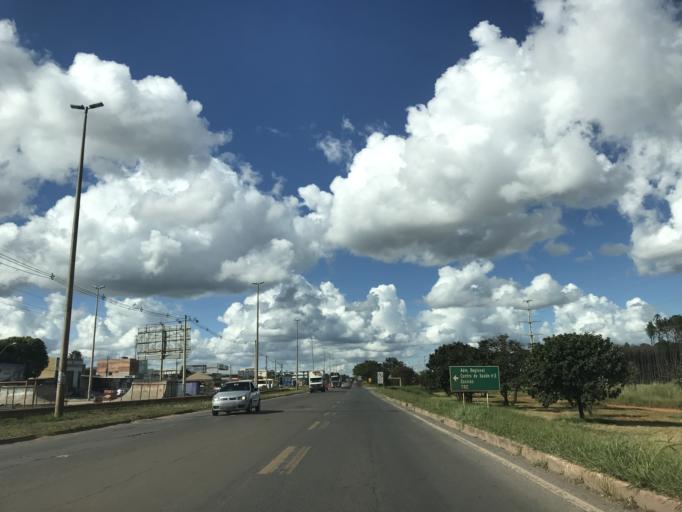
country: BR
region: Federal District
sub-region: Brasilia
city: Brasilia
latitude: -15.7539
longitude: -47.7656
